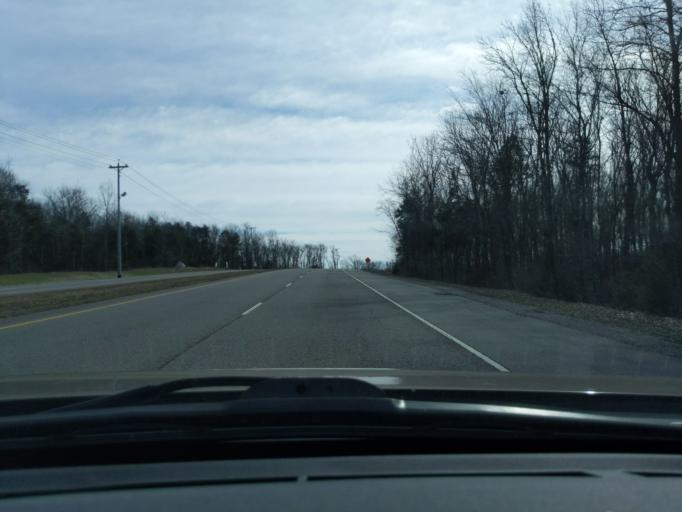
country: US
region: Tennessee
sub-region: Wilson County
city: Mount Juliet
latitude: 36.1835
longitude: -86.4596
